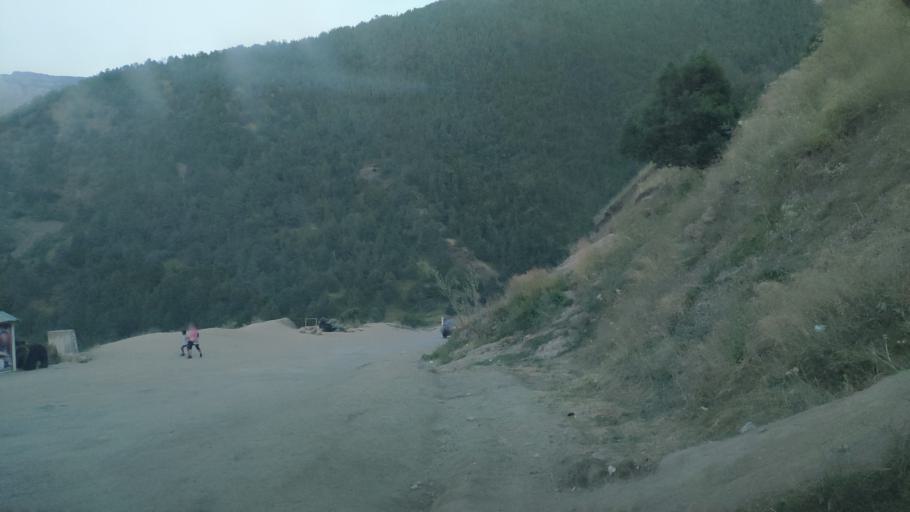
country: TJ
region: Viloyati Sughd
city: Ayni
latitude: 39.6321
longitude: 68.4919
